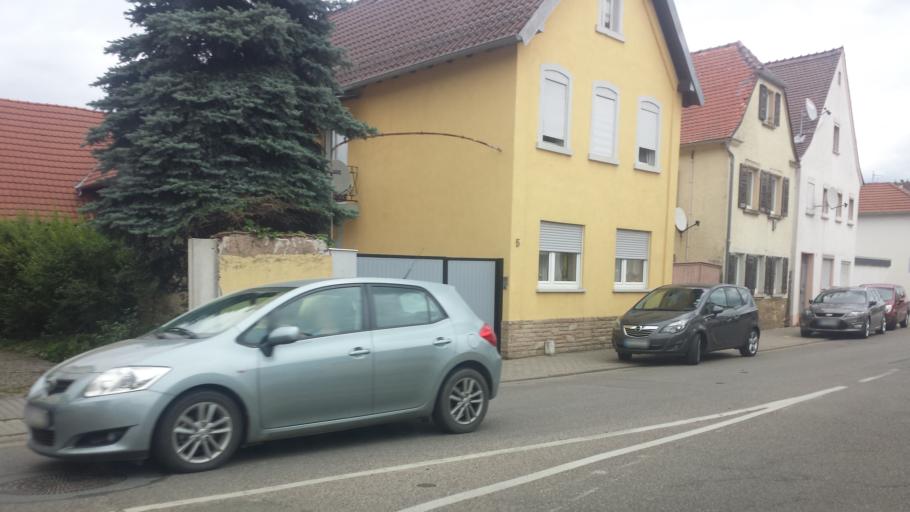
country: DE
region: Rheinland-Pfalz
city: Meckenheim
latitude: 49.4038
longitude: 8.2405
